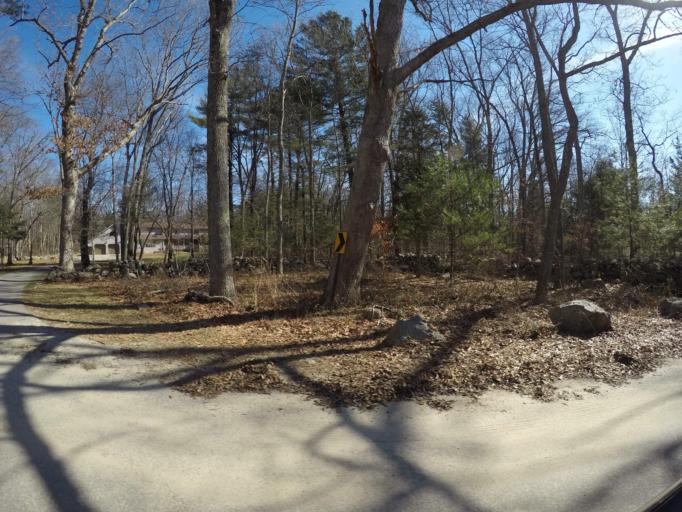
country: US
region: Massachusetts
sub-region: Bristol County
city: Easton
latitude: 42.0752
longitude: -71.1476
